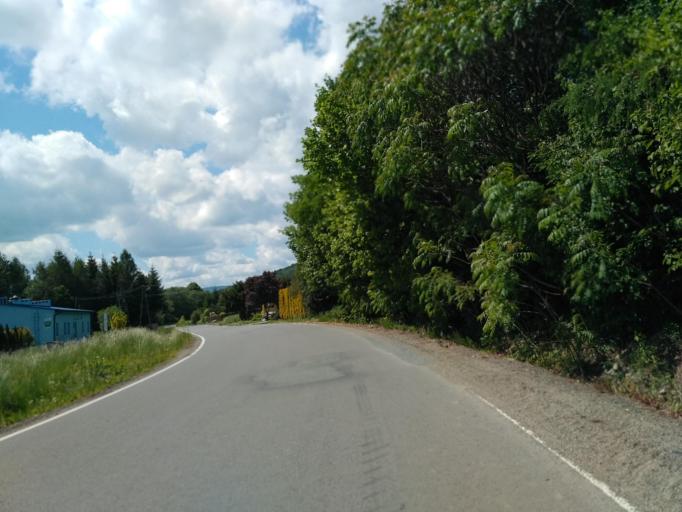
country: PL
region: Subcarpathian Voivodeship
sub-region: Powiat krosnienski
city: Dukla
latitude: 49.5986
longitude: 21.7039
